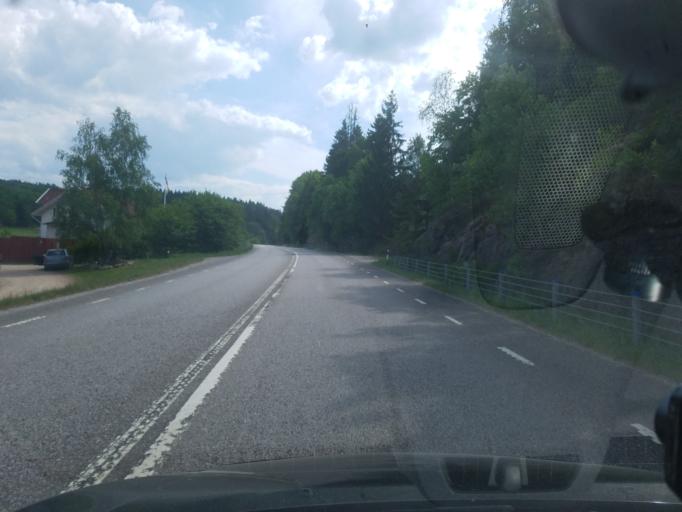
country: SE
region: Vaestra Goetaland
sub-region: Orust
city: Henan
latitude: 58.1906
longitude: 11.6896
